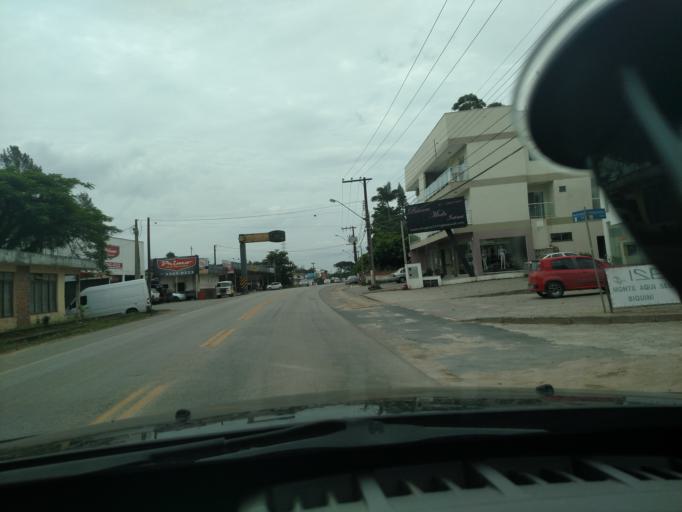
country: BR
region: Santa Catarina
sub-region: Gaspar
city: Gaspar
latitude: -26.8934
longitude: -48.8222
